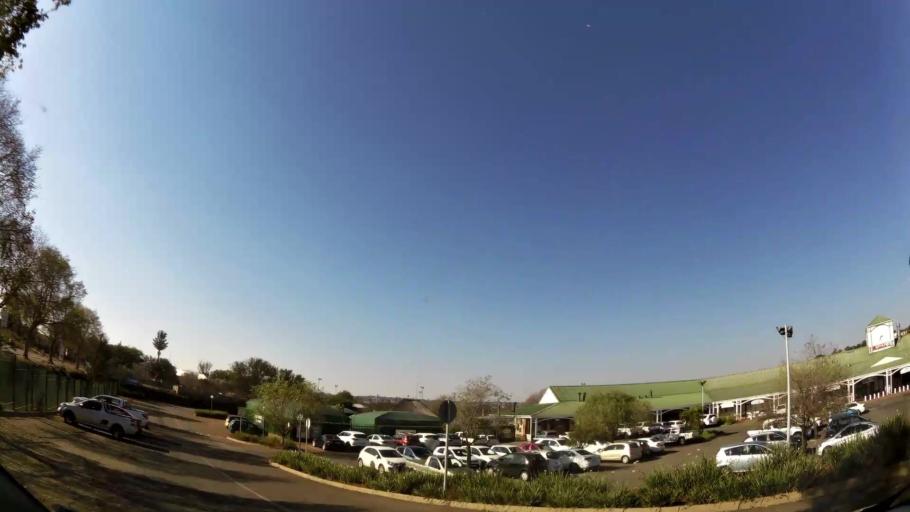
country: ZA
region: Gauteng
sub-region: City of Tshwane Metropolitan Municipality
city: Centurion
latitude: -25.8542
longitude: 28.1686
